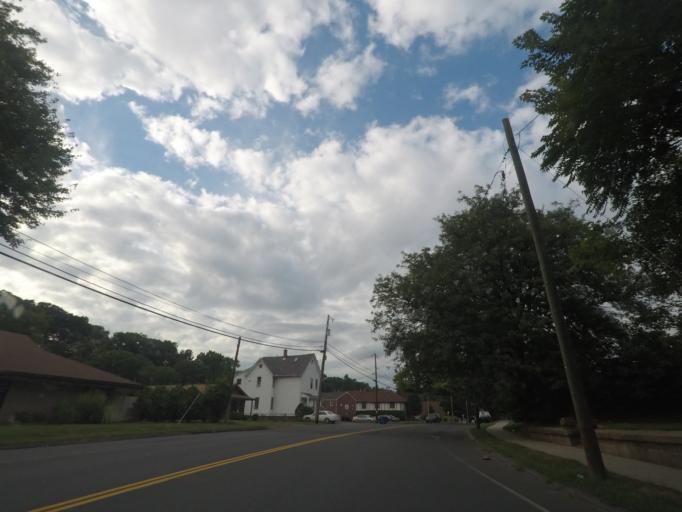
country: US
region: Massachusetts
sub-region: Hampden County
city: West Springfield
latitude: 42.1169
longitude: -72.6275
